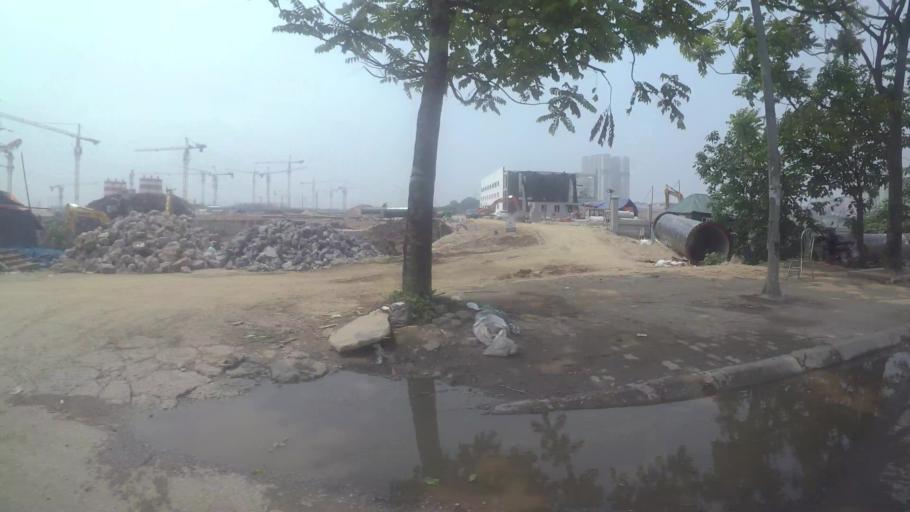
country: VN
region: Ha Noi
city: Cau Dien
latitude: 21.0099
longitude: 105.7360
